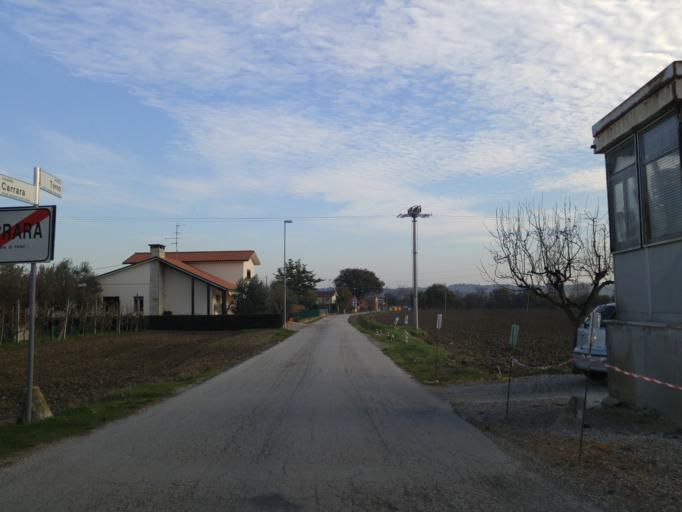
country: IT
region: The Marches
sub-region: Provincia di Pesaro e Urbino
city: Cuccurano
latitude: 43.7914
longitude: 12.9575
